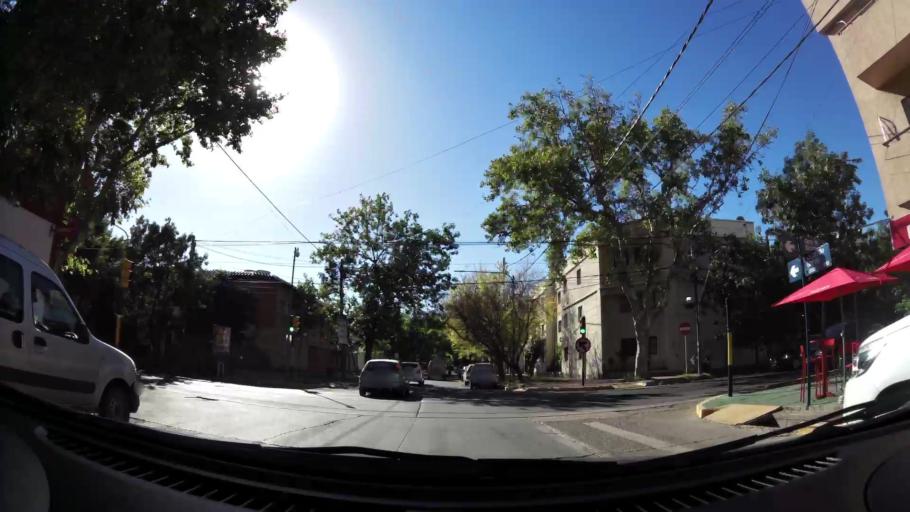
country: AR
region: Mendoza
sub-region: Departamento de Godoy Cruz
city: Godoy Cruz
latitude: -32.9159
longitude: -68.8427
